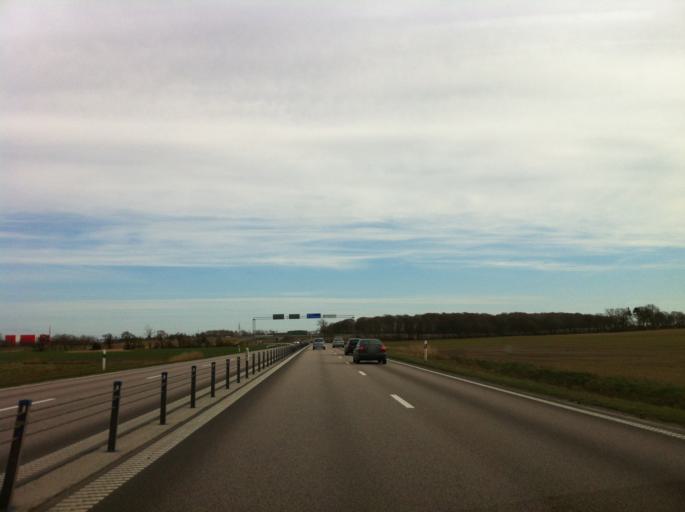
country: SE
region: Skane
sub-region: Helsingborg
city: Odakra
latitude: 56.0892
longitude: 12.7083
